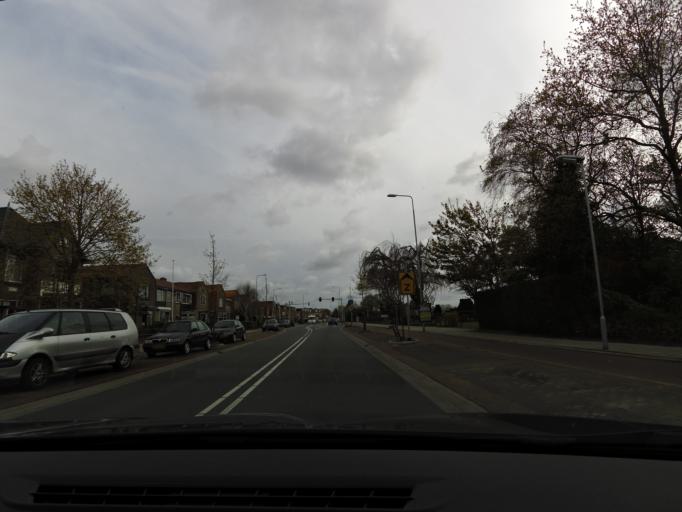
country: NL
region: South Holland
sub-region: Gemeente Hillegom
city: Hillegom
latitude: 52.2836
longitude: 4.5729
